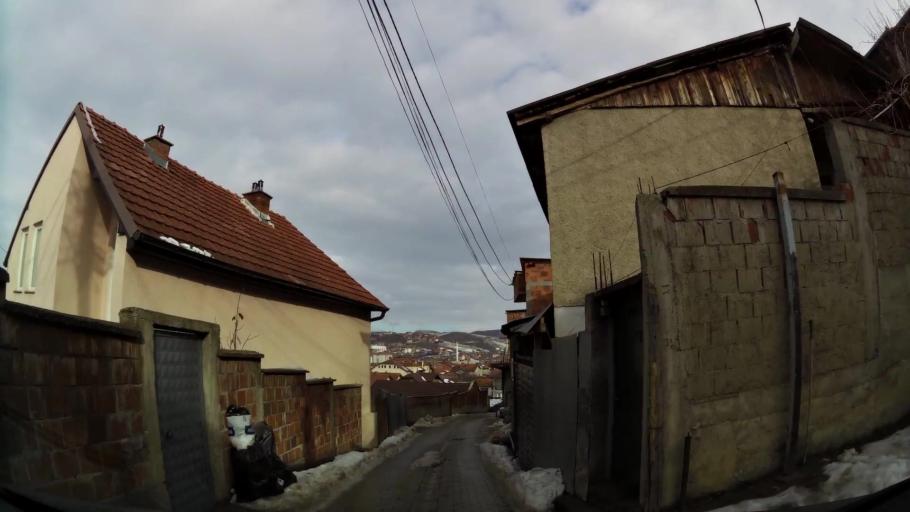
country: XK
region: Pristina
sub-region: Komuna e Prishtines
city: Pristina
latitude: 42.6772
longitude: 21.1760
